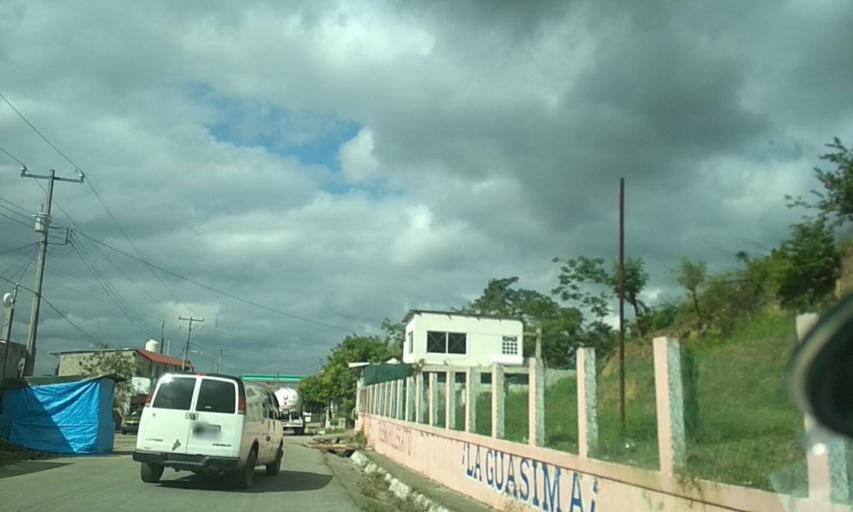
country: MX
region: Veracruz
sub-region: Papantla
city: Polutla
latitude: 20.5400
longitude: -97.2502
